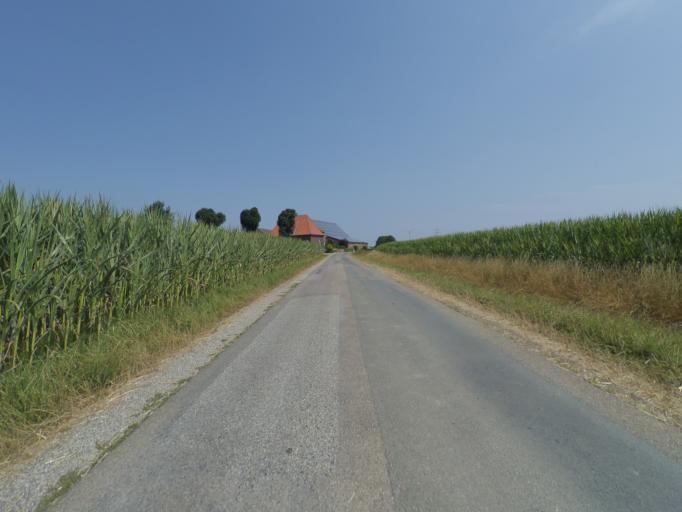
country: DE
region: North Rhine-Westphalia
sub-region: Regierungsbezirk Dusseldorf
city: Mehrhoog
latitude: 51.7396
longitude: 6.4682
